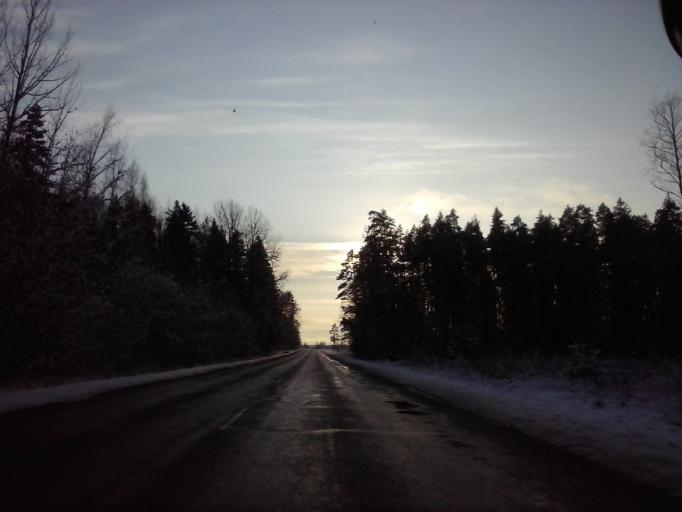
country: EE
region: Tartu
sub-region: UElenurme vald
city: Ulenurme
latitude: 58.3316
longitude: 26.8915
